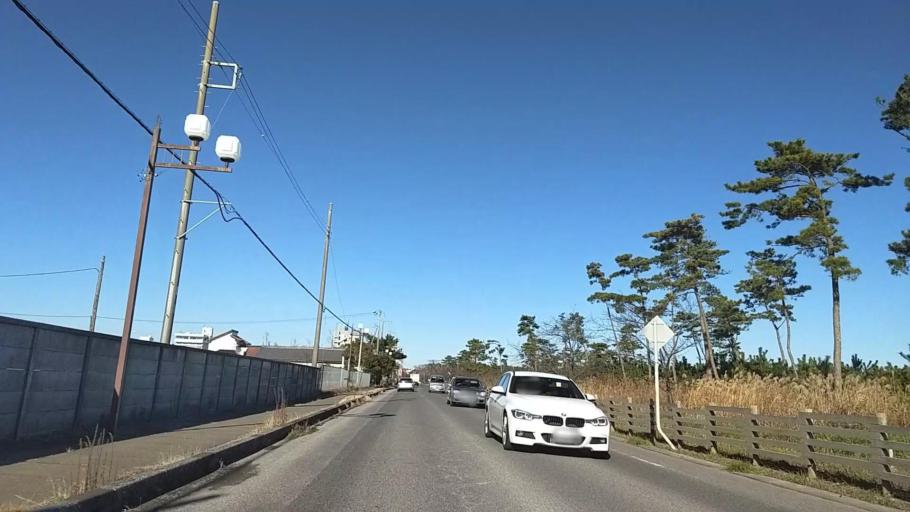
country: JP
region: Chiba
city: Mobara
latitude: 35.4246
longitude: 140.3943
